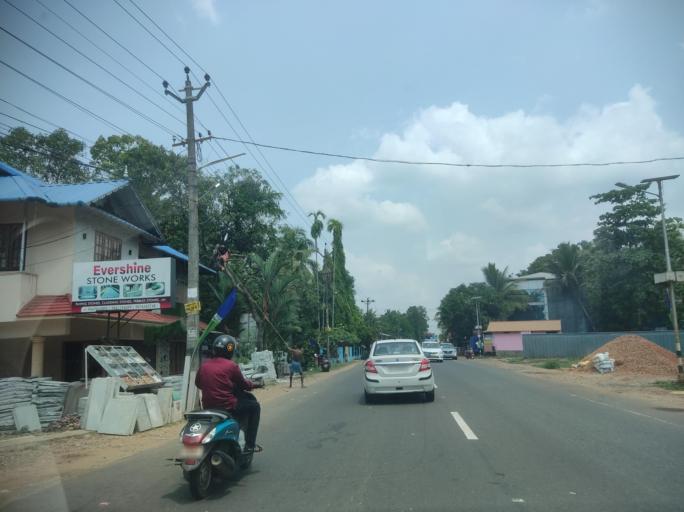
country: IN
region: Kerala
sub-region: Kottayam
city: Changanacheri
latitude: 9.4176
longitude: 76.5491
